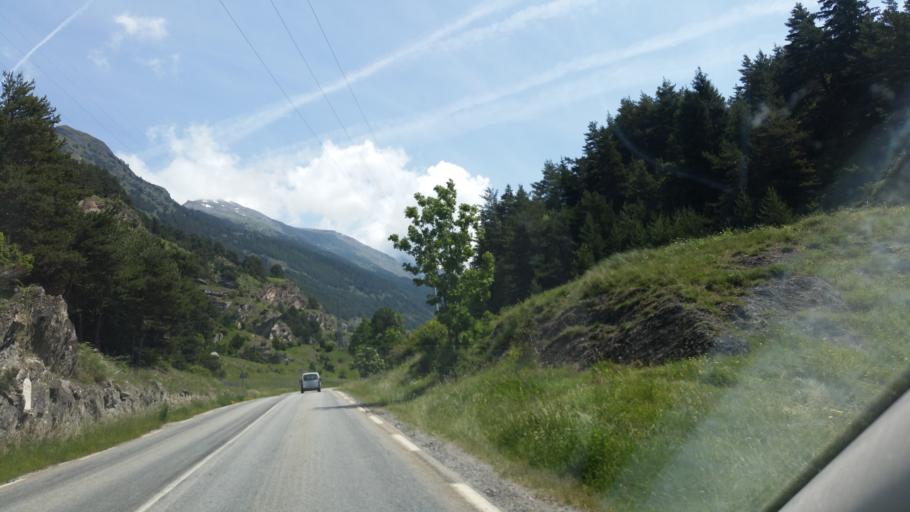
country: FR
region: Rhone-Alpes
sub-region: Departement de la Savoie
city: Modane
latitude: 45.2796
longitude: 6.8207
